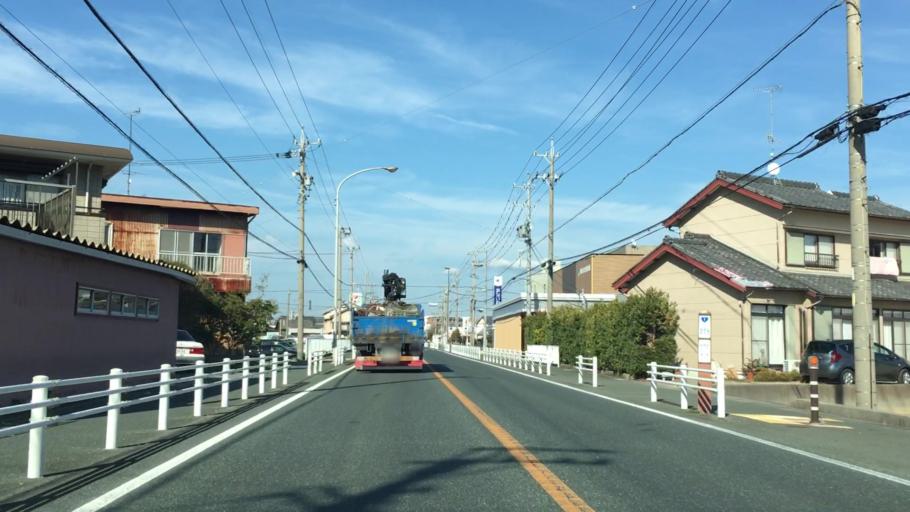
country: JP
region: Shizuoka
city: Kosai-shi
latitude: 34.6899
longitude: 137.5632
